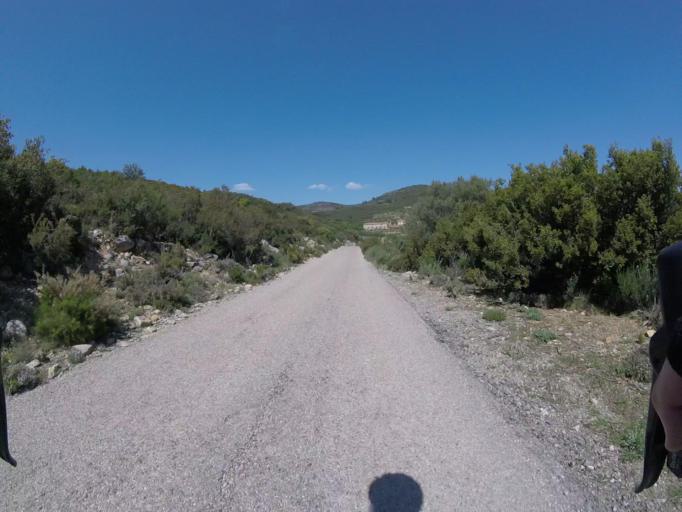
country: ES
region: Valencia
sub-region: Provincia de Castello
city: Sierra-Engarceran
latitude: 40.2467
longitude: -0.0286
